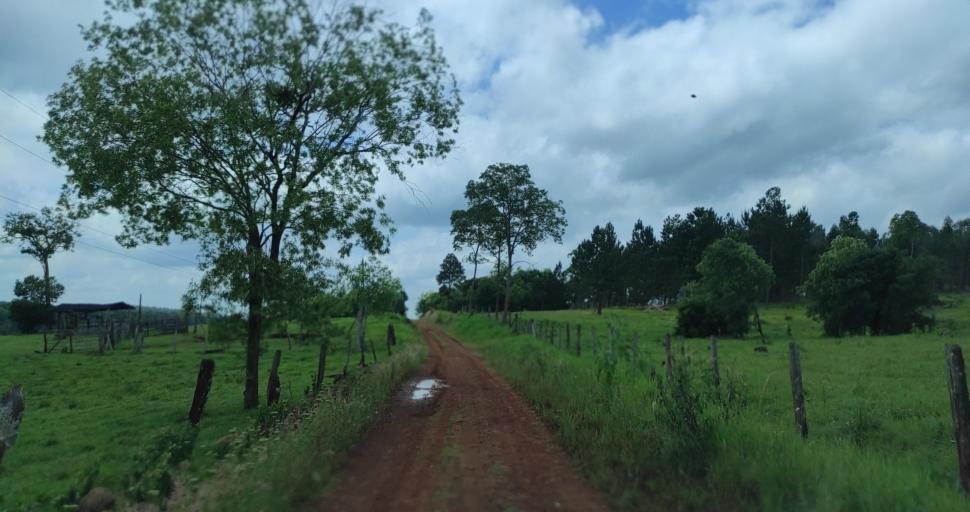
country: AR
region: Misiones
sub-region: Departamento de Veinticinco de Mayo
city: Veinticinco de Mayo
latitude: -27.4150
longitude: -54.7254
